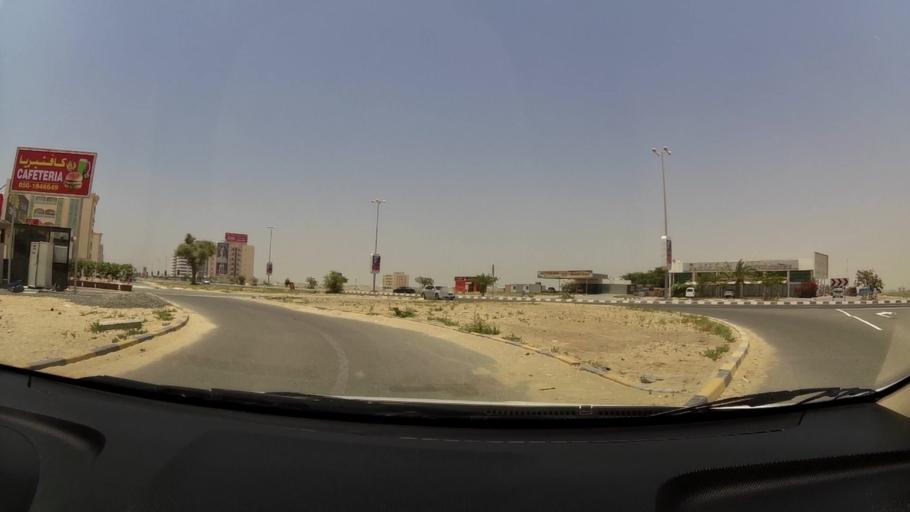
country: AE
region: Umm al Qaywayn
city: Umm al Qaywayn
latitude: 25.5137
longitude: 55.5449
